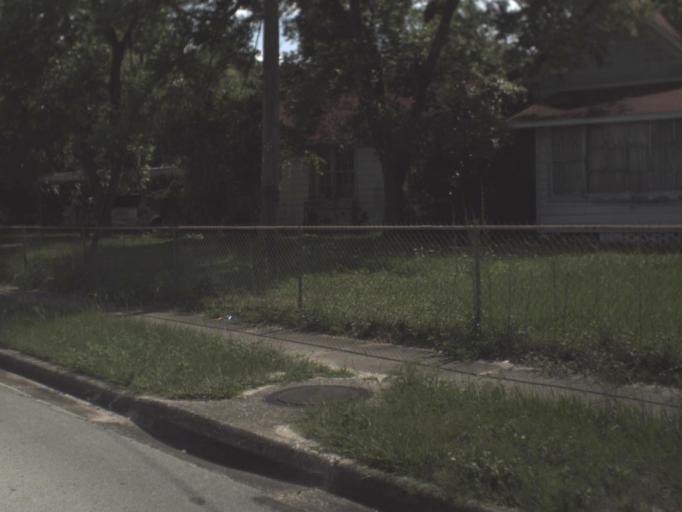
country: US
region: Florida
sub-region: Alachua County
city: Hawthorne
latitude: 29.5851
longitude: -82.0853
